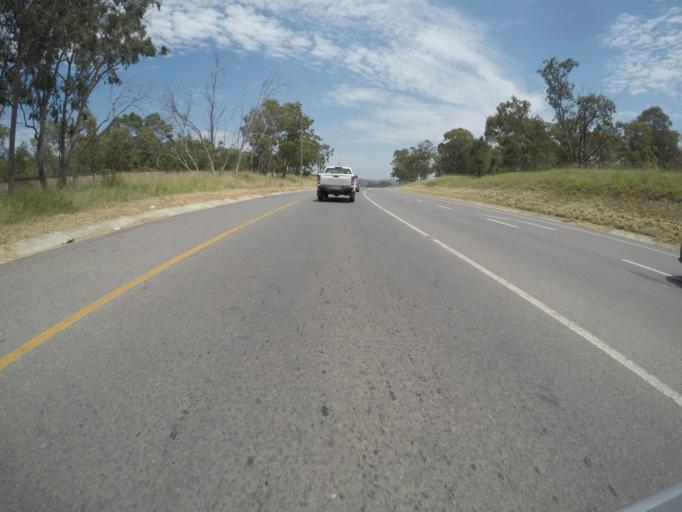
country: ZA
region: Eastern Cape
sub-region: Buffalo City Metropolitan Municipality
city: East London
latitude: -32.9392
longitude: 27.9523
